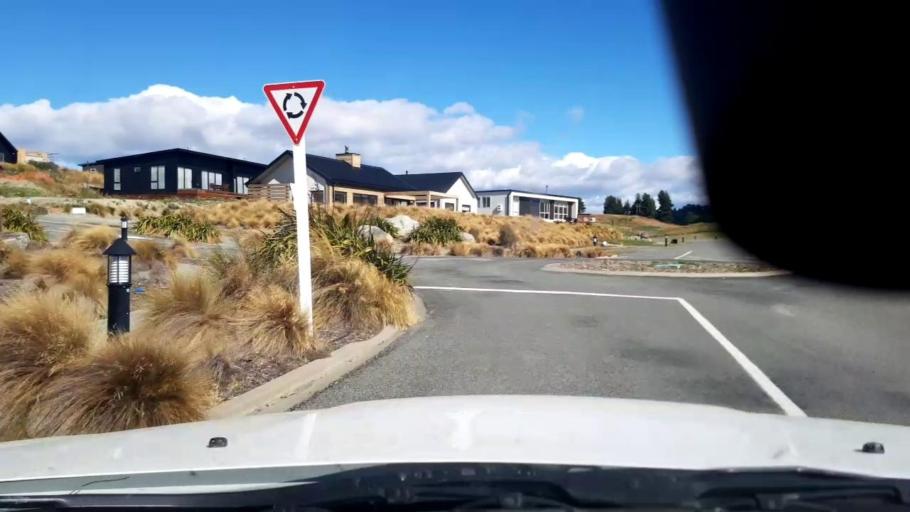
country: NZ
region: Canterbury
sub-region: Timaru District
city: Pleasant Point
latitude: -44.0055
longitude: 170.4721
